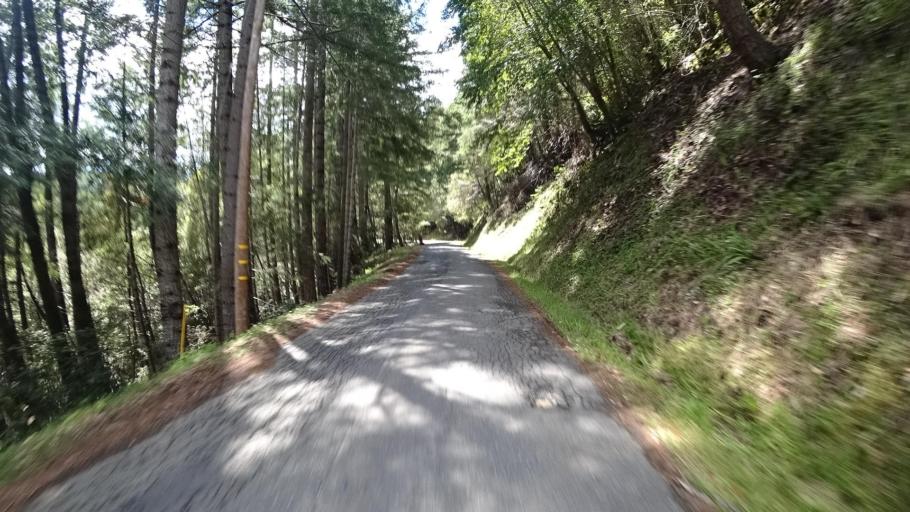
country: US
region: California
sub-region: Humboldt County
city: Blue Lake
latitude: 40.7628
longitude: -123.9480
